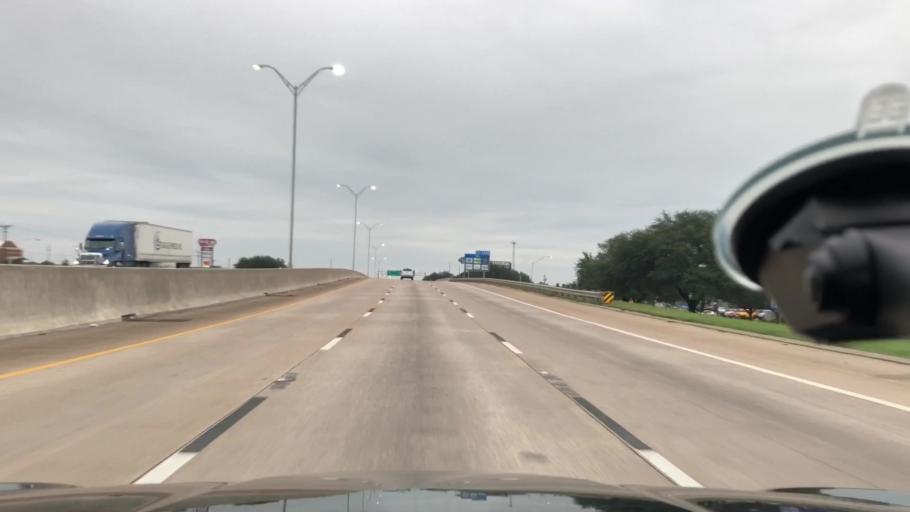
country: US
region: Texas
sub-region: McLennan County
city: Beverly
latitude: 31.5192
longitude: -97.1364
